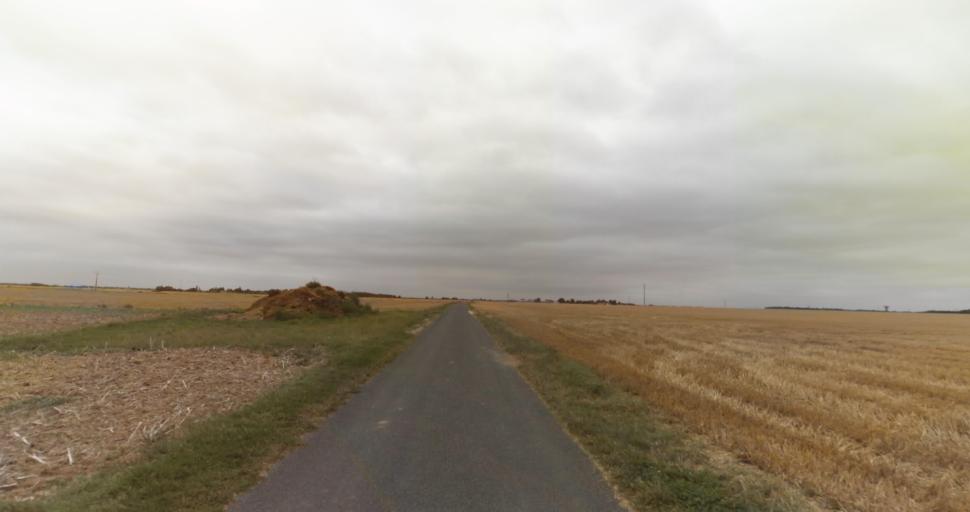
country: FR
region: Haute-Normandie
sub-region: Departement de l'Eure
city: La Couture-Boussey
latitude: 48.9422
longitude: 1.3377
